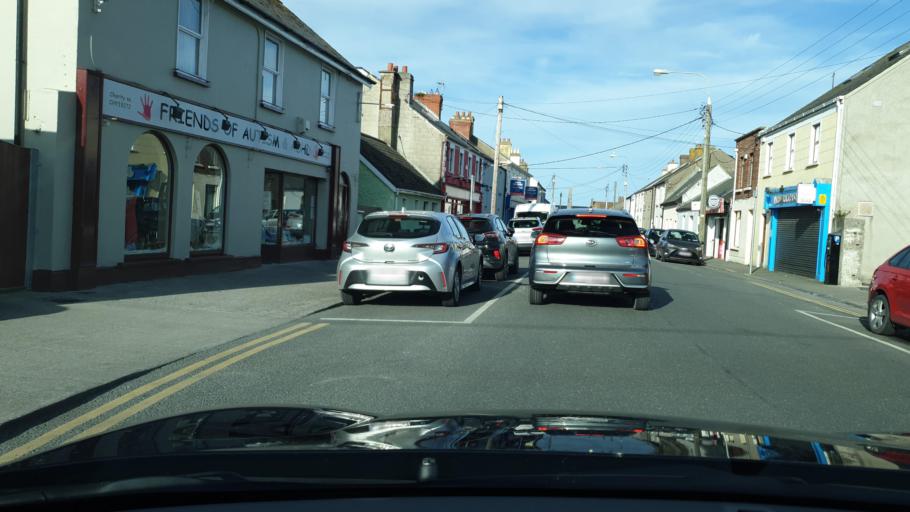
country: IE
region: Leinster
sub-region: Fingal County
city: Skerries
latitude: 53.5803
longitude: -6.1094
